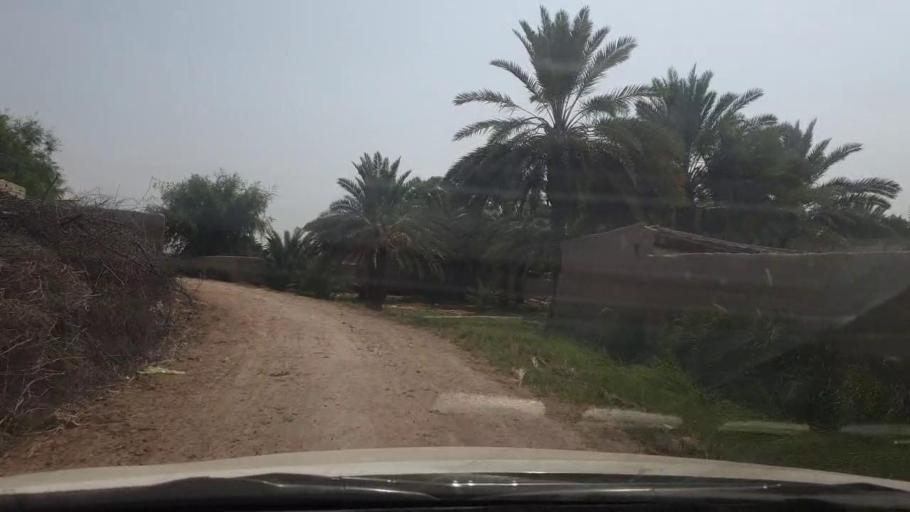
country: PK
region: Sindh
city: Khairpur
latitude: 27.5623
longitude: 68.8409
